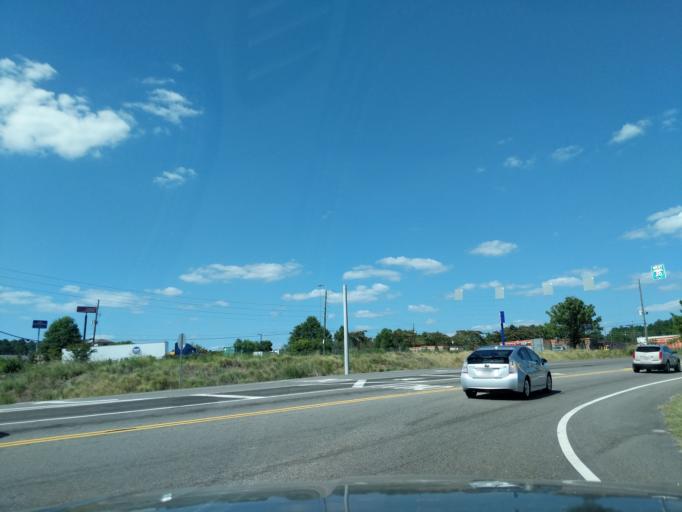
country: US
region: Georgia
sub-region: Columbia County
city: Martinez
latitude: 33.5224
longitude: -82.0324
